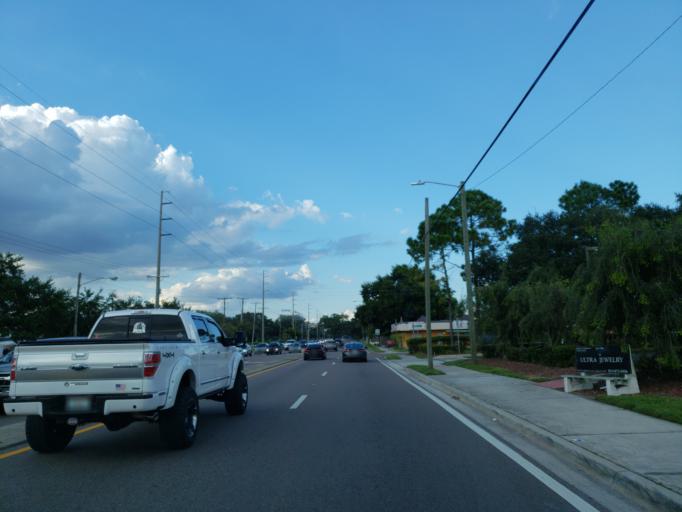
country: US
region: Florida
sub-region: Hillsborough County
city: Tampa
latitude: 27.9670
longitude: -82.5014
